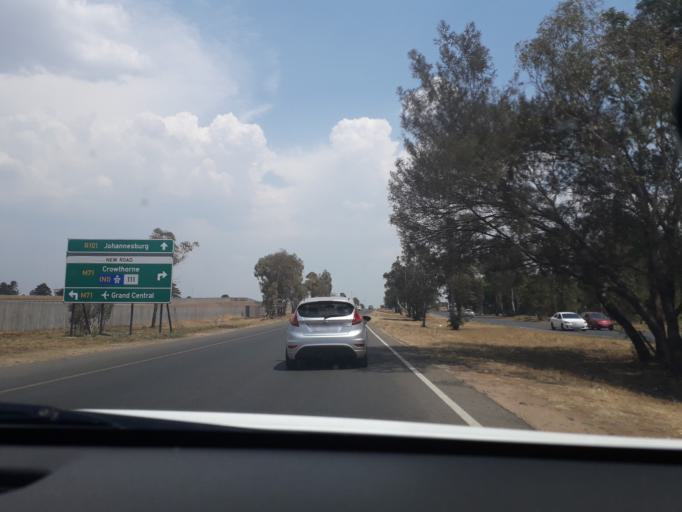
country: ZA
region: Gauteng
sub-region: City of Johannesburg Metropolitan Municipality
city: Midrand
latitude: -25.9786
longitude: 28.1341
